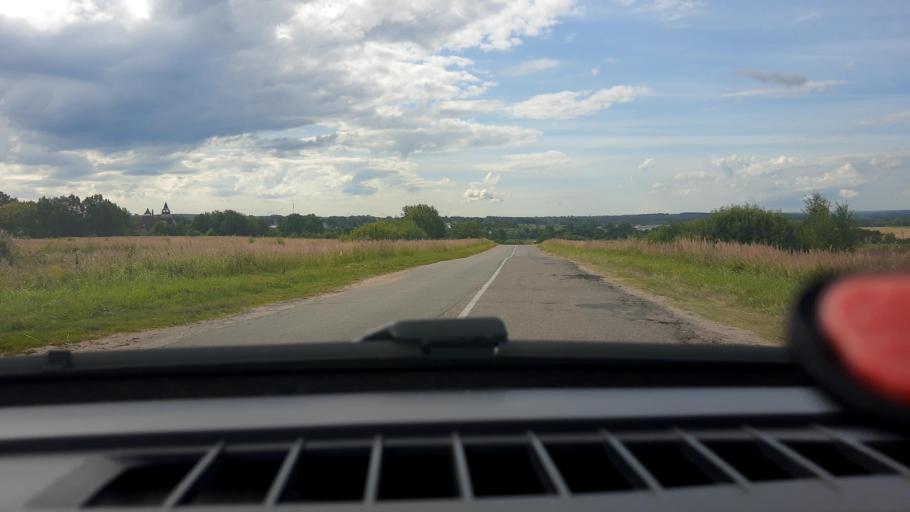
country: RU
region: Nizjnij Novgorod
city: Burevestnik
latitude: 56.0442
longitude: 43.7144
